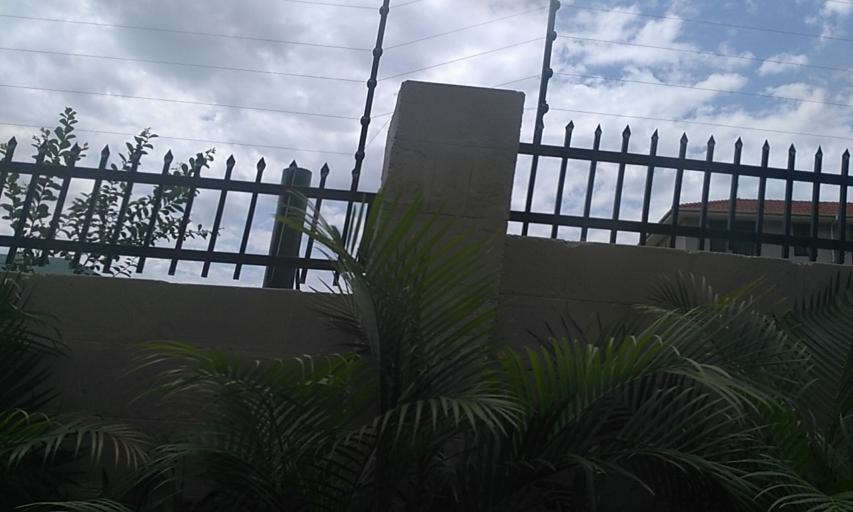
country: UG
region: Central Region
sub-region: Kampala District
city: Kampala
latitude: 0.3317
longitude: 32.5924
